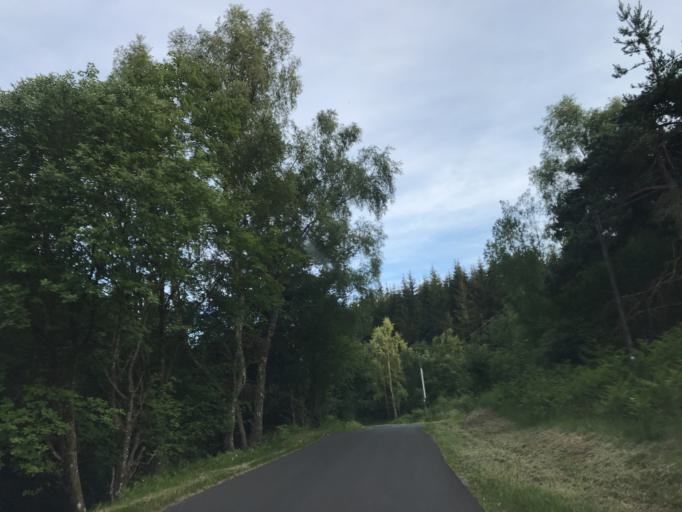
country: FR
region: Rhone-Alpes
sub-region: Departement de la Loire
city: Noiretable
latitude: 45.7815
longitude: 3.6891
